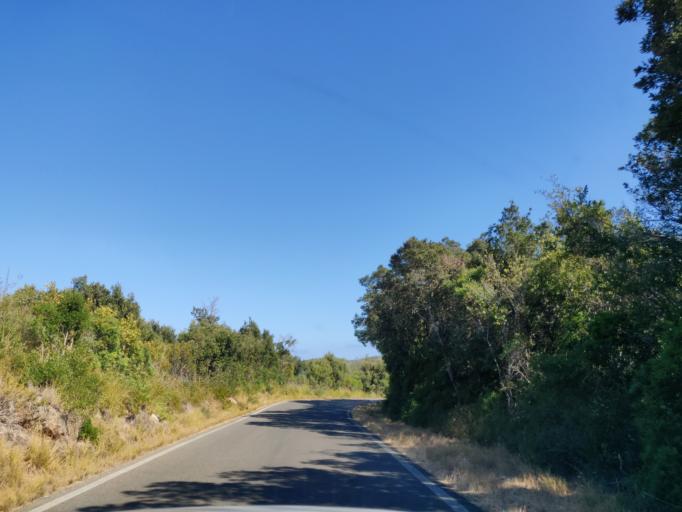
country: IT
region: Tuscany
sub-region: Provincia di Grosseto
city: Porto Ercole
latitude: 42.4278
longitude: 11.1724
